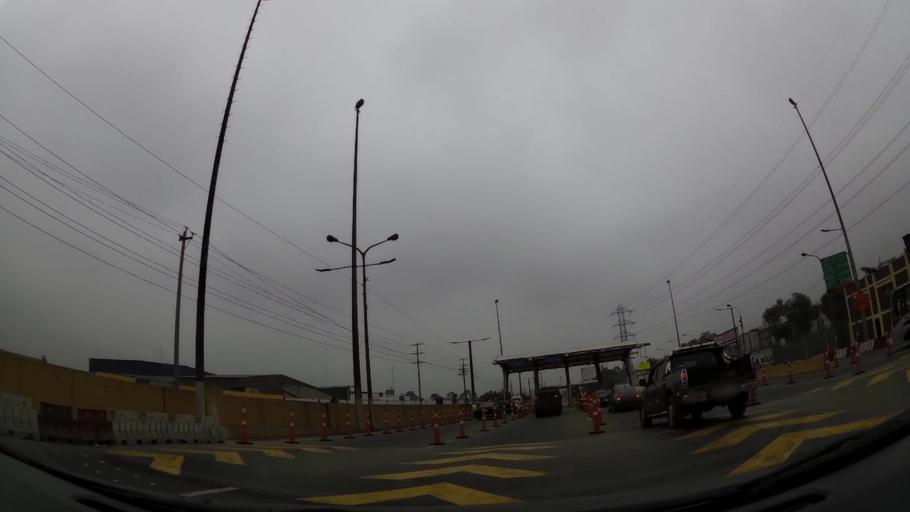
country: PE
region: Lima
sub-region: Lima
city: Urb. Santo Domingo
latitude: -11.9097
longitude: -77.0713
